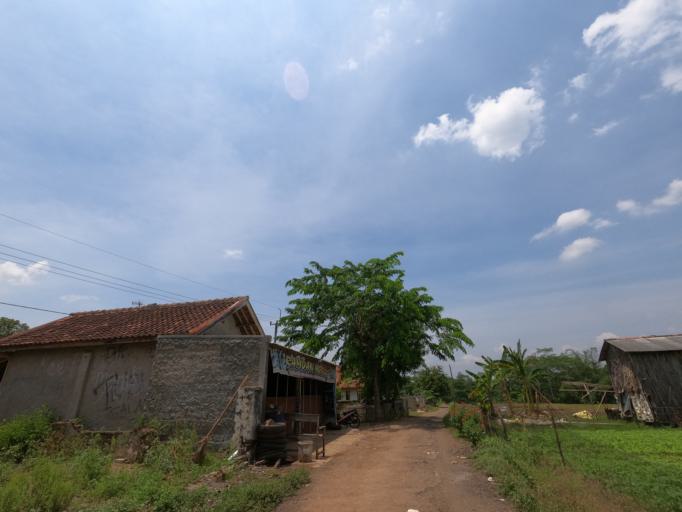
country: ID
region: West Java
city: Pamanukan
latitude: -6.5126
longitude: 107.7722
